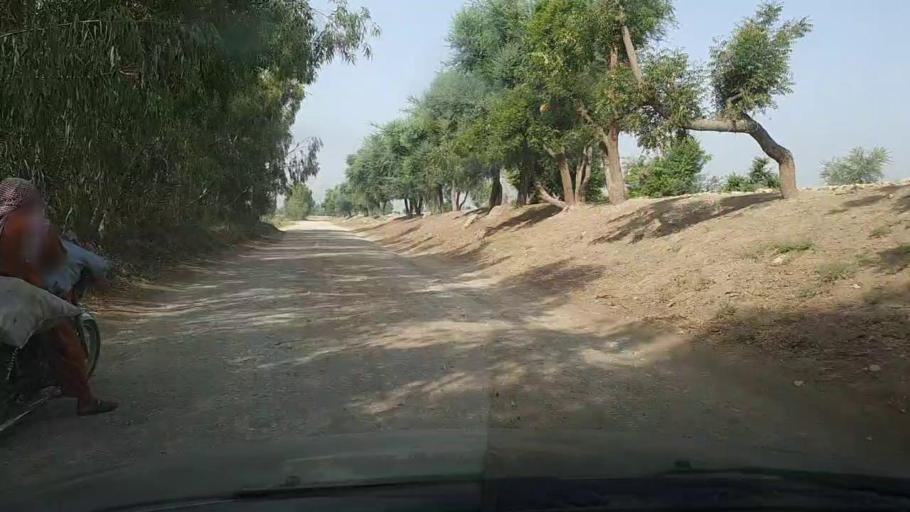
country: PK
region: Sindh
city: Pir jo Goth
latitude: 27.5238
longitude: 68.4888
